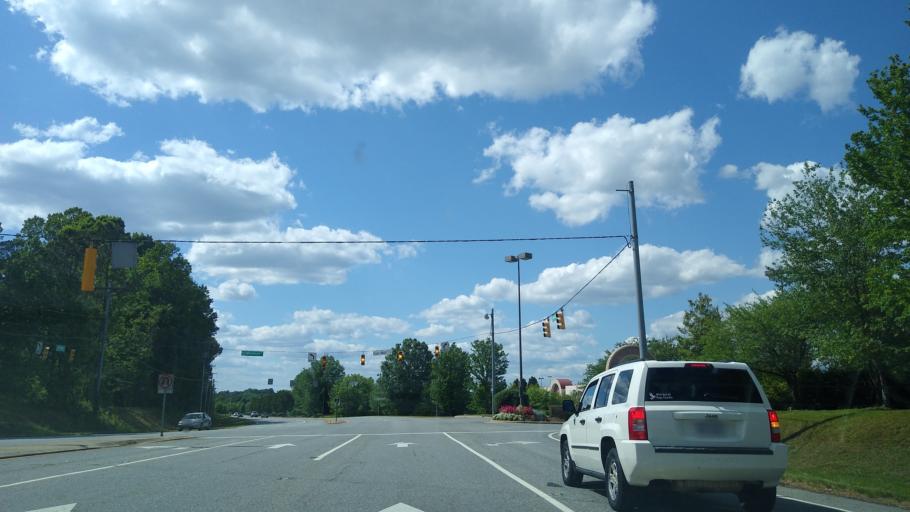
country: US
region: North Carolina
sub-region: Guilford County
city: High Point
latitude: 35.9875
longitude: -80.0060
